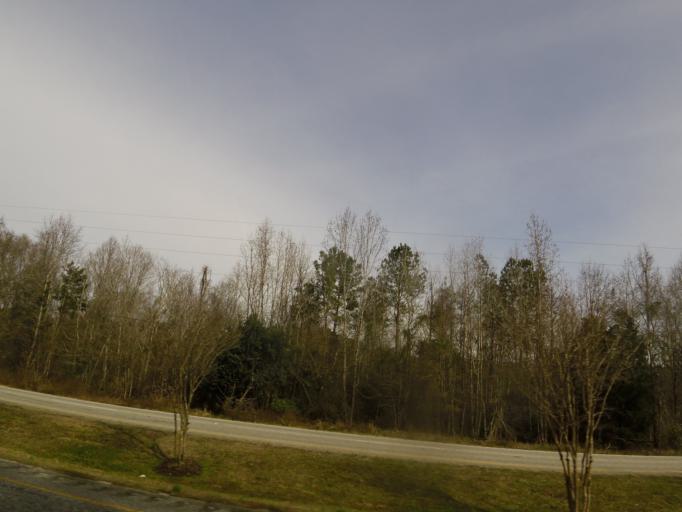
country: US
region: Alabama
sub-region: Dale County
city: Ozark
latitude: 31.4543
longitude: -85.6640
